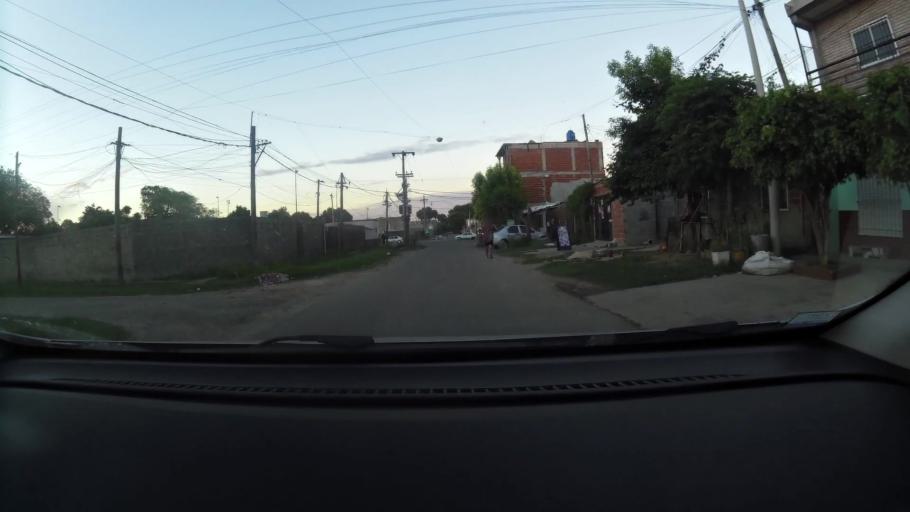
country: AR
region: Santa Fe
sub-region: Departamento de Rosario
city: Rosario
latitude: -32.9607
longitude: -60.6860
